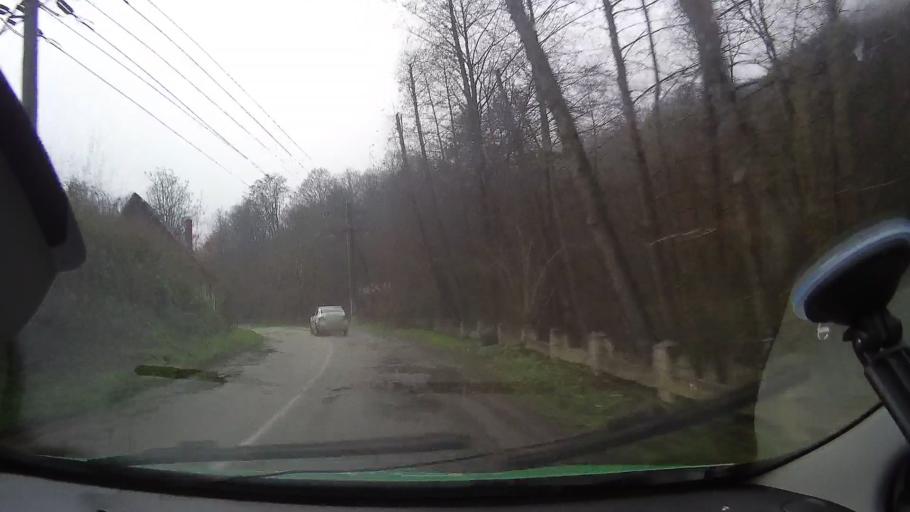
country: RO
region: Arad
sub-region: Comuna Dezna
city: Dezna
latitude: 46.4130
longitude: 22.2550
